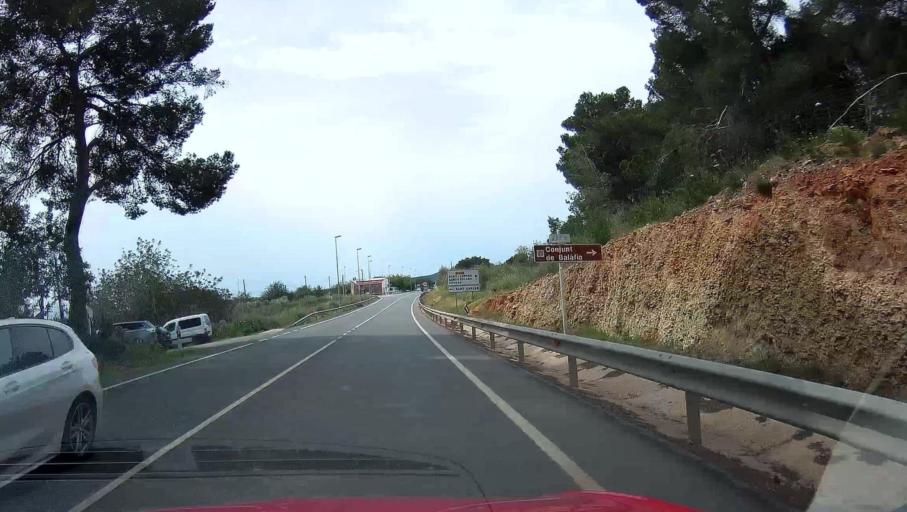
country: ES
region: Balearic Islands
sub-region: Illes Balears
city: Sant Joan de Labritja
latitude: 39.0354
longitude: 1.4911
